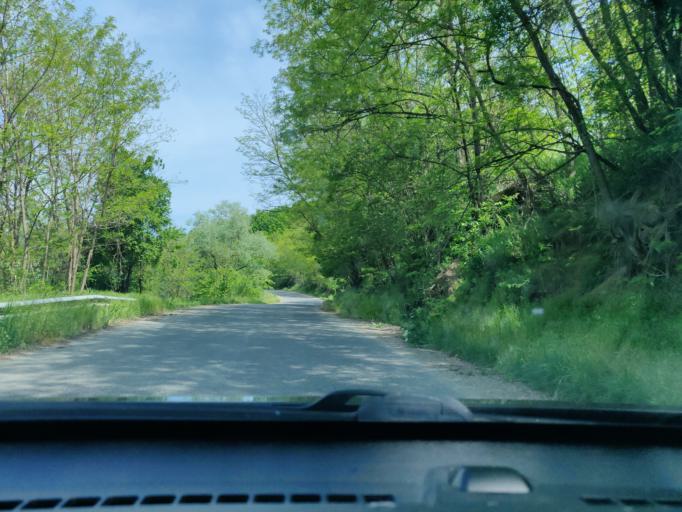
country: RO
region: Vrancea
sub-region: Comuna Vidra
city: Vidra
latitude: 45.9272
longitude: 26.8961
